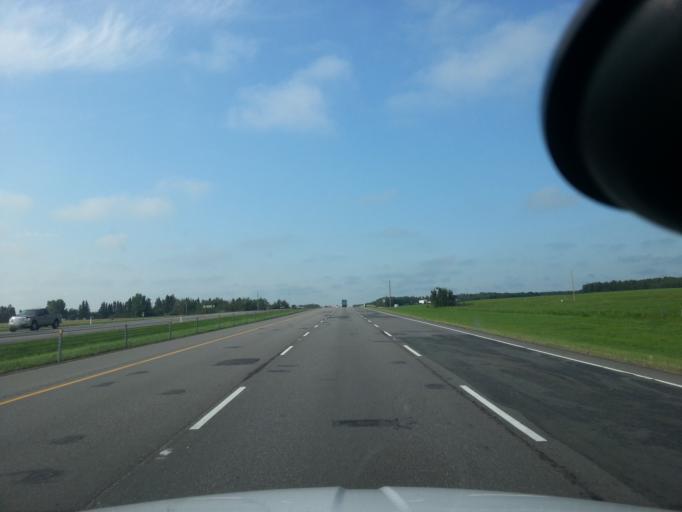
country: CA
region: Alberta
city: Penhold
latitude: 52.0837
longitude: -113.8589
